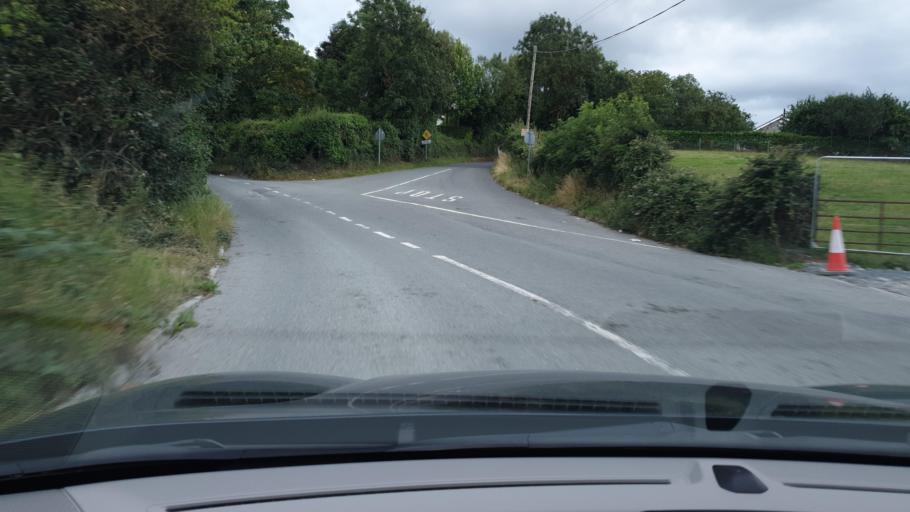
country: IE
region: Leinster
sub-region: South Dublin
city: Saggart
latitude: 53.2750
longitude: -6.4504
